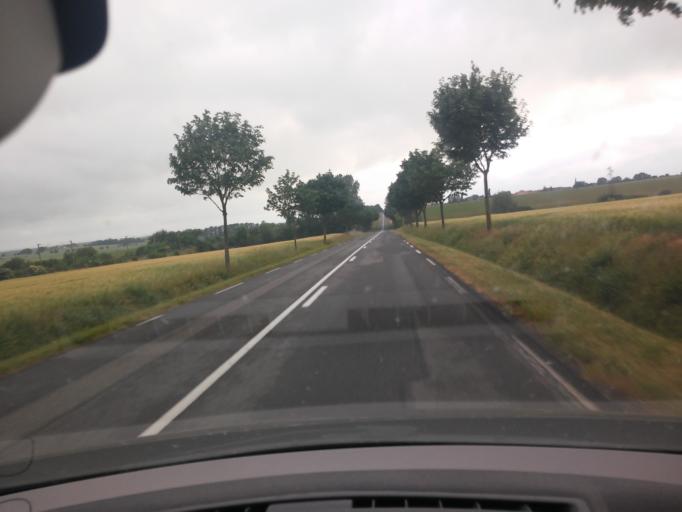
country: FR
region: Lorraine
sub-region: Departement de Meurthe-et-Moselle
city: Doncourt-les-Conflans
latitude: 49.0671
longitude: 5.8881
